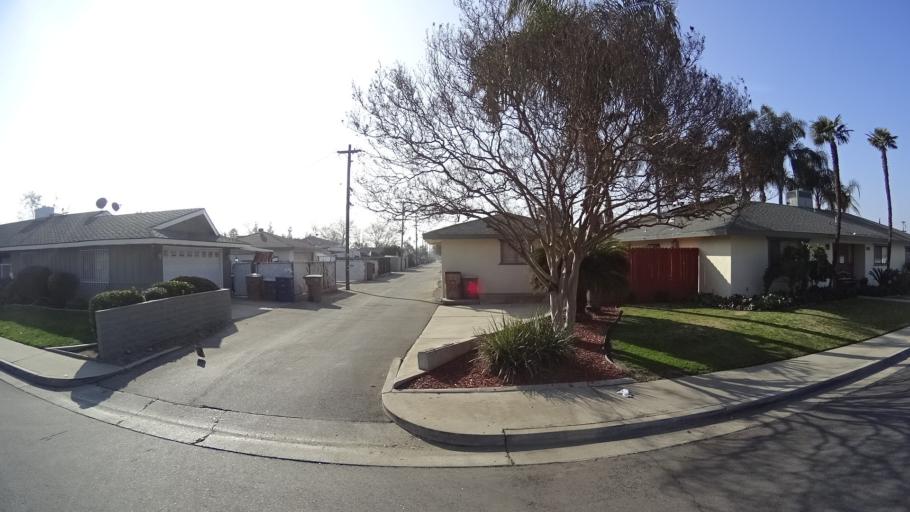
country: US
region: California
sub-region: Kern County
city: Bakersfield
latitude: 35.3282
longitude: -119.0308
